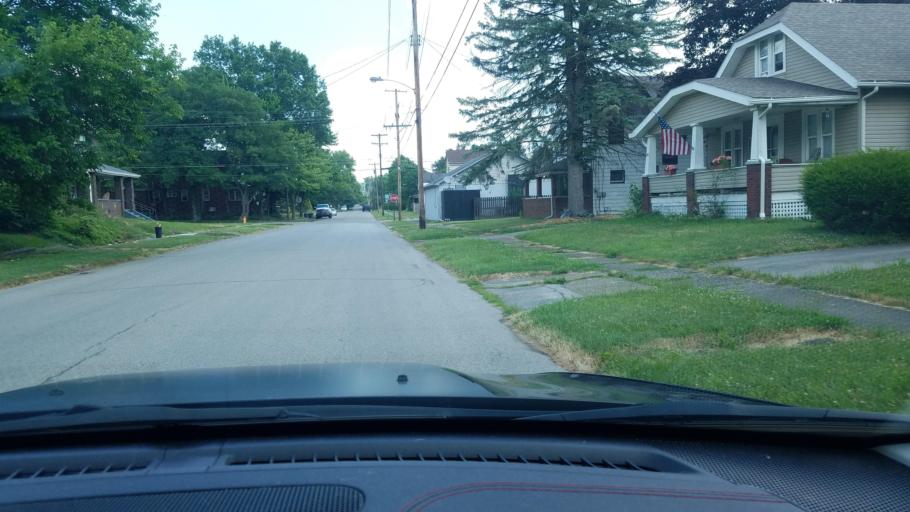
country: US
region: Ohio
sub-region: Mahoning County
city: Campbell
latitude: 41.0775
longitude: -80.5947
